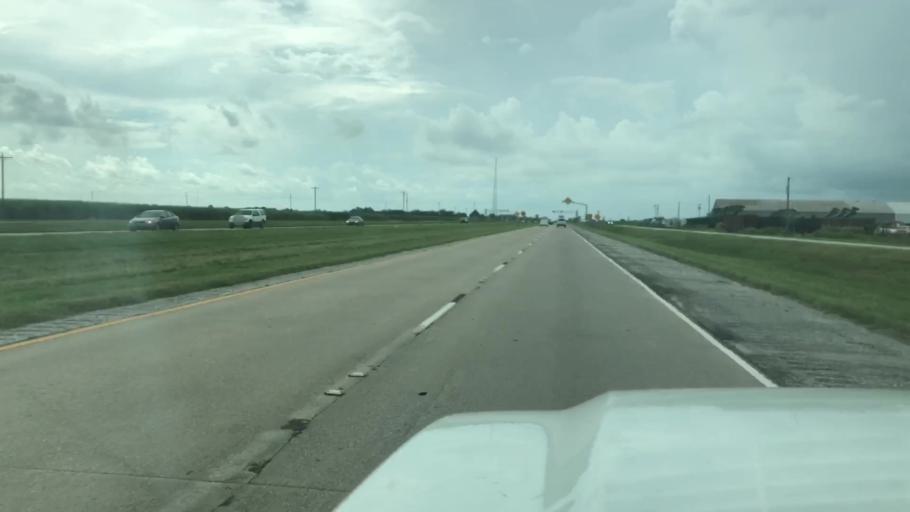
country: US
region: Louisiana
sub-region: Iberia Parish
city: Jeanerette
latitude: 29.9102
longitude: -91.7141
